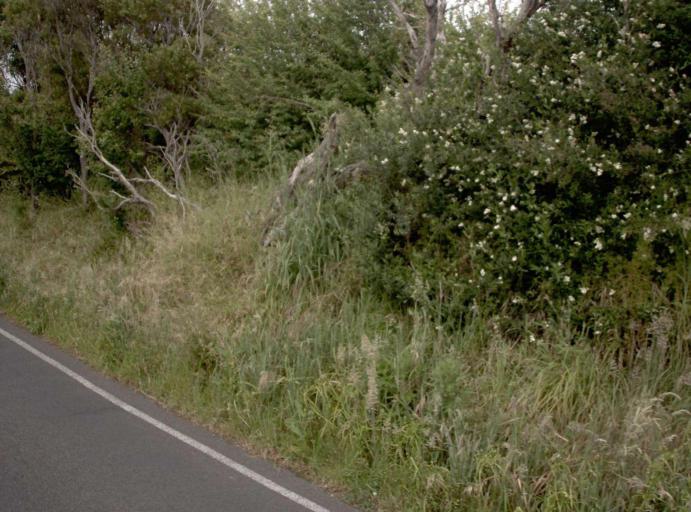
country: AU
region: Victoria
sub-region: Bass Coast
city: North Wonthaggi
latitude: -38.5038
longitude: 145.7255
